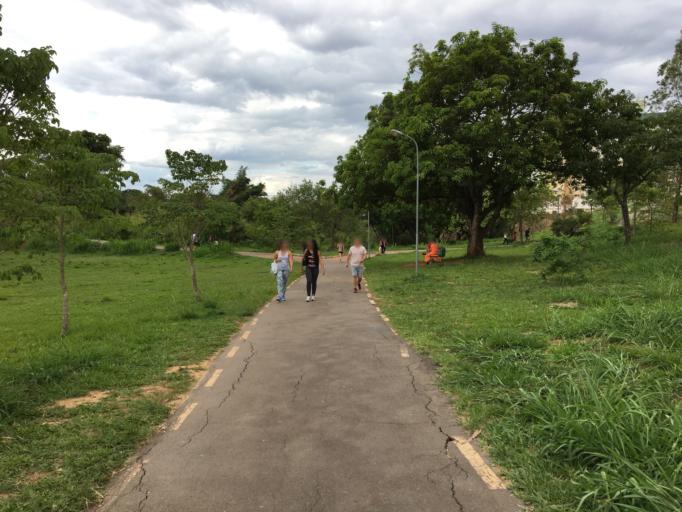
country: BR
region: Federal District
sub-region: Brasilia
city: Brasilia
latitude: -15.8314
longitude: -48.0200
